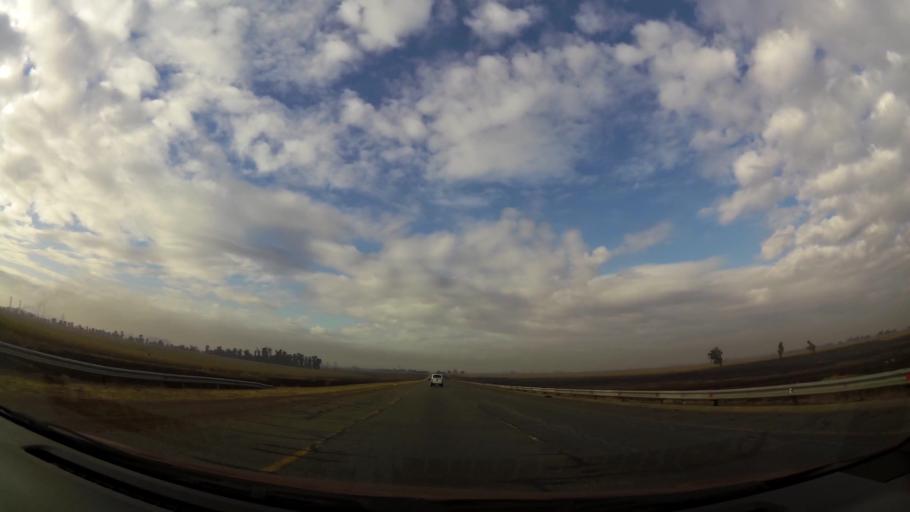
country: ZA
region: Gauteng
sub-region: Sedibeng District Municipality
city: Vanderbijlpark
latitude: -26.6506
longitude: 27.7804
